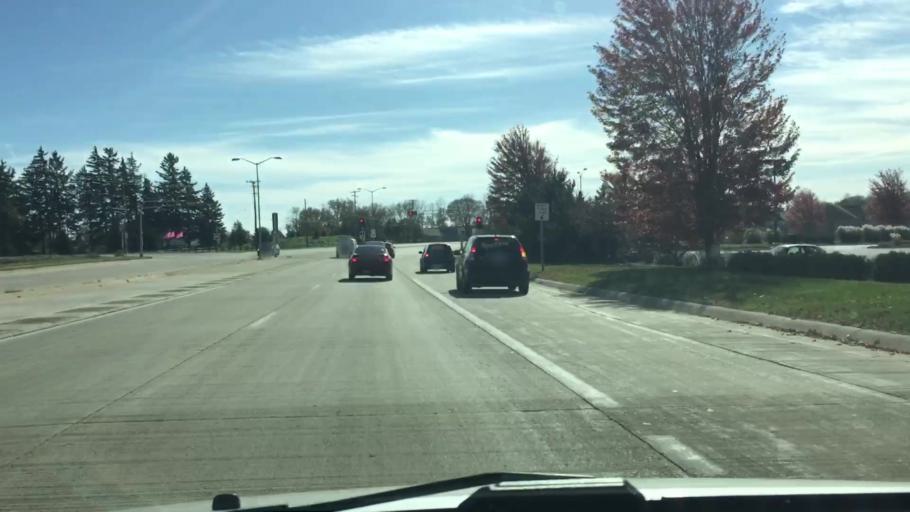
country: US
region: Wisconsin
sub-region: Waukesha County
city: Pewaukee
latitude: 43.0876
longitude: -88.2265
